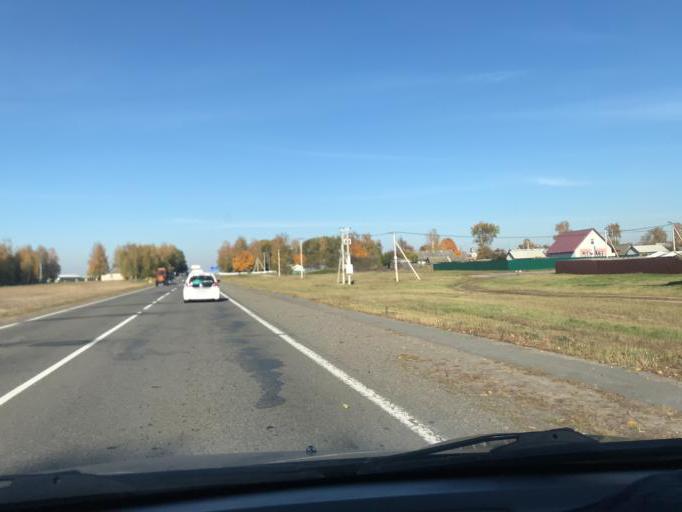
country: BY
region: Gomel
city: Parychy
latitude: 52.6241
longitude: 29.3774
